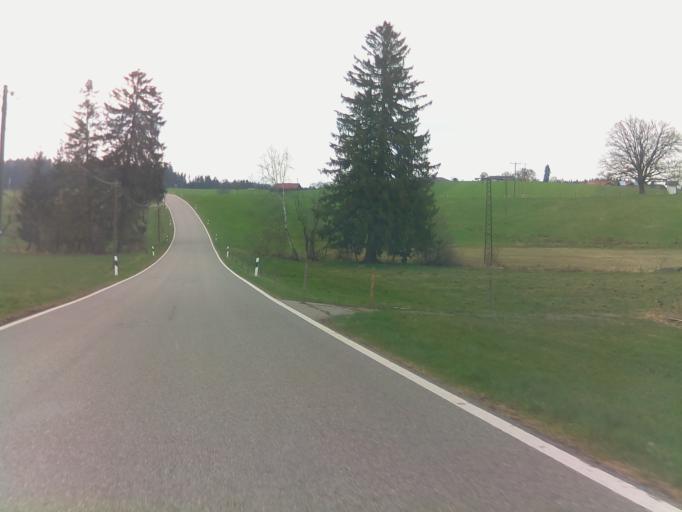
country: DE
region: Bavaria
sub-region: Upper Bavaria
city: Obersochering
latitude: 47.7528
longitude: 11.2227
